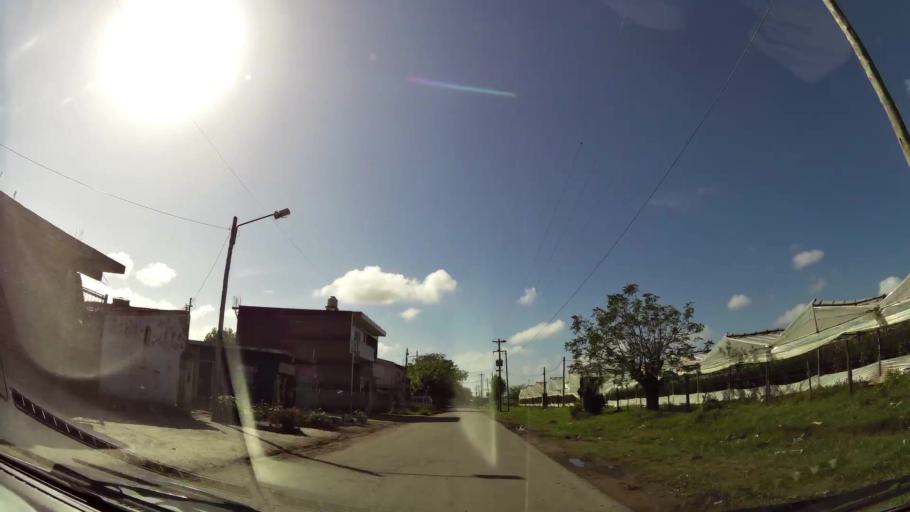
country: AR
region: Buenos Aires
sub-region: Partido de Quilmes
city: Quilmes
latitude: -34.7980
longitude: -58.1394
